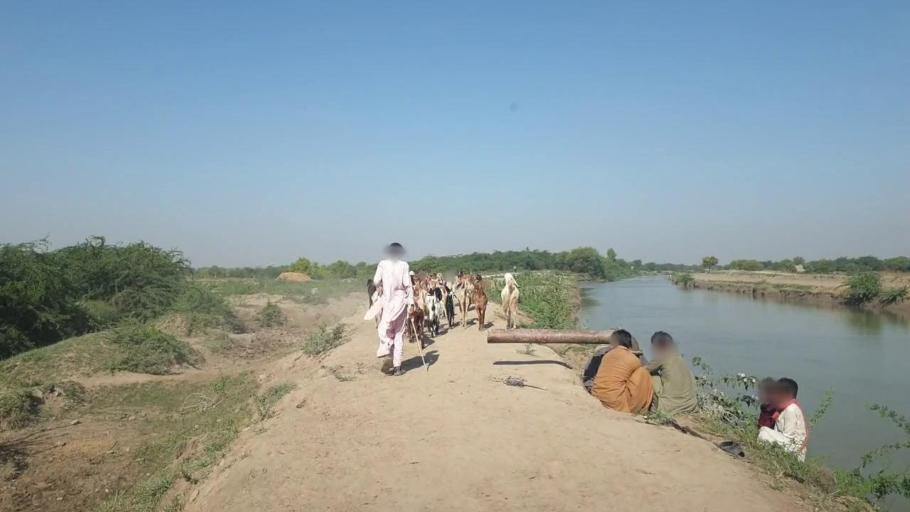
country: PK
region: Sindh
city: Talhar
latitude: 24.7981
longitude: 68.7953
